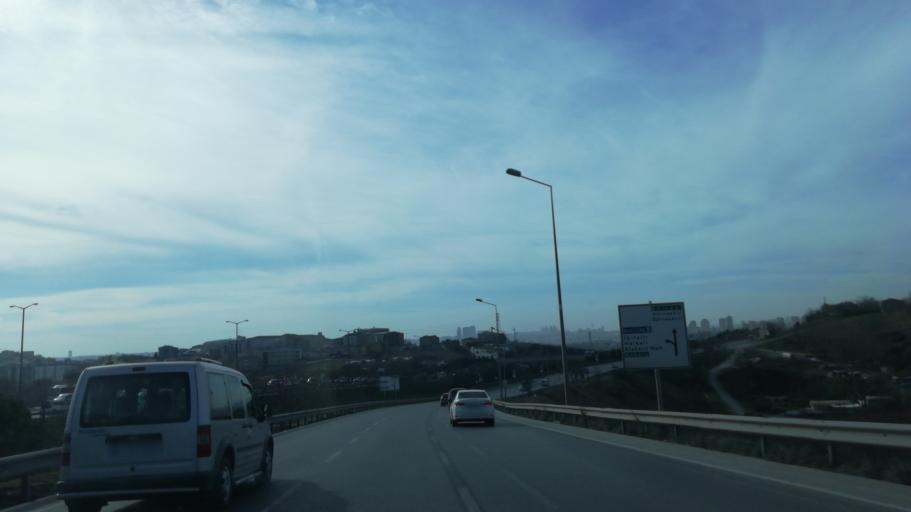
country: TR
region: Istanbul
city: Basaksehir
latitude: 41.0624
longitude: 28.7595
